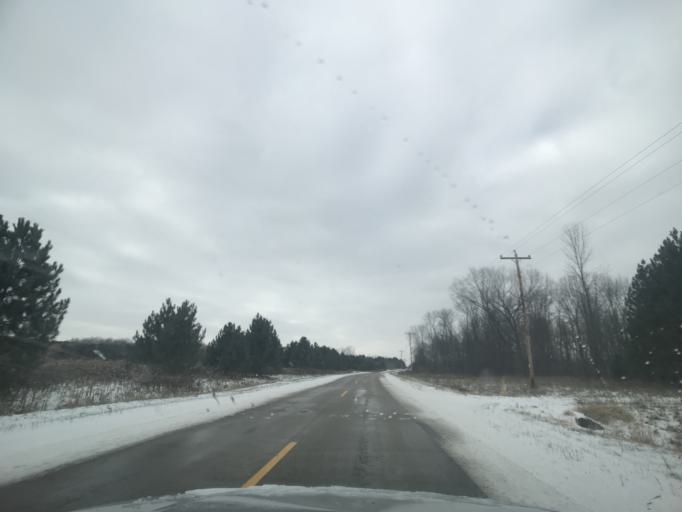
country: US
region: Wisconsin
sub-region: Brown County
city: Suamico
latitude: 44.7059
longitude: -88.0787
